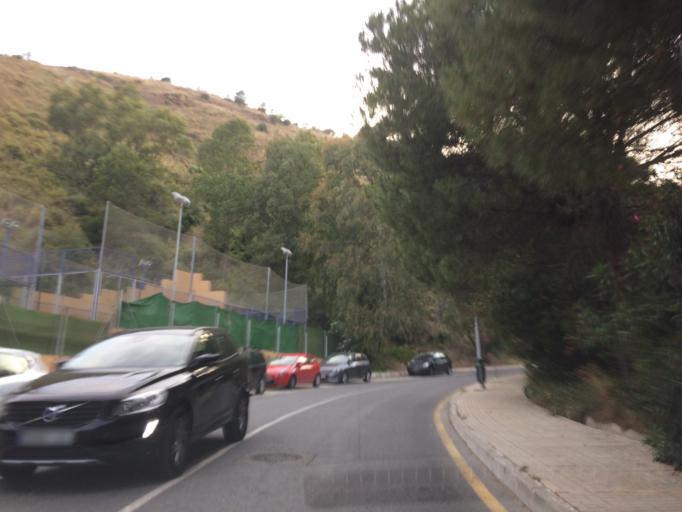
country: ES
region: Andalusia
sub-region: Provincia de Malaga
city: Malaga
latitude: 36.7330
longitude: -4.4040
